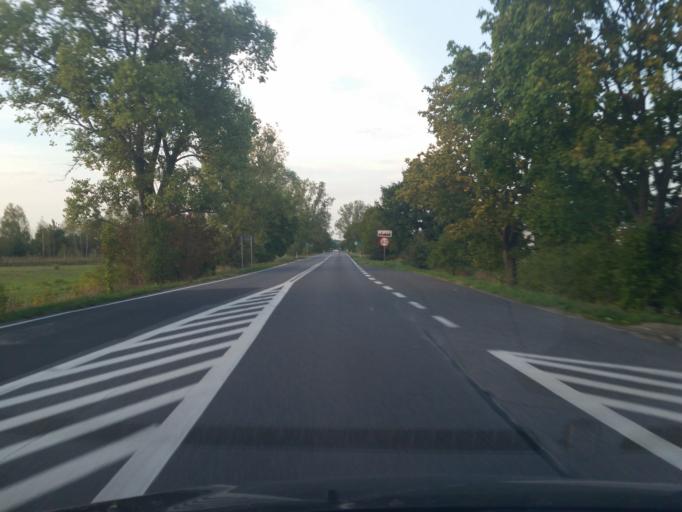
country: PL
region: Masovian Voivodeship
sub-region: Powiat nowodworski
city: Zakroczym
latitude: 52.3803
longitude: 20.6302
